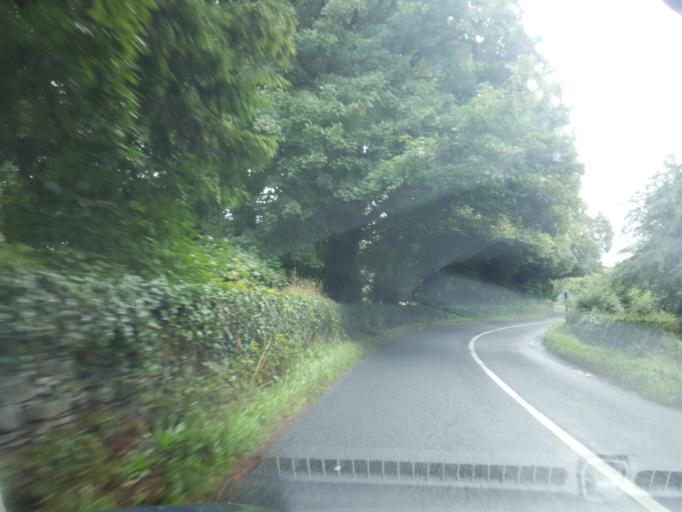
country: IE
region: Leinster
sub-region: Kildare
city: Kilcullen
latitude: 53.1262
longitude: -6.7342
